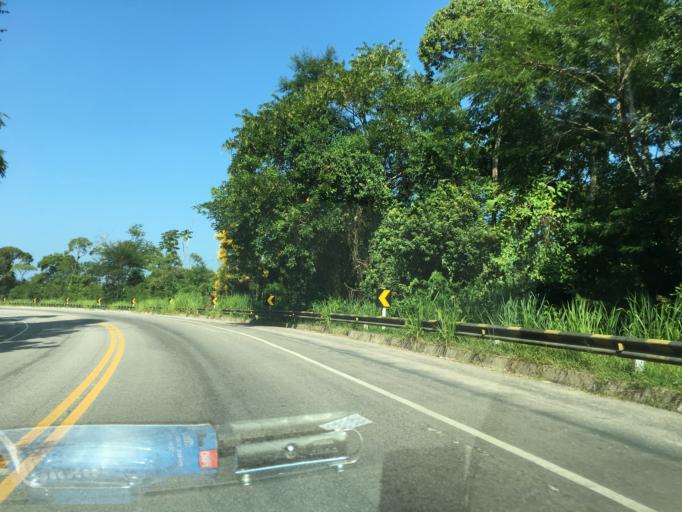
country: BR
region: Sao Paulo
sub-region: Ubatuba
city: Ubatuba
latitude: -23.4140
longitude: -45.0559
